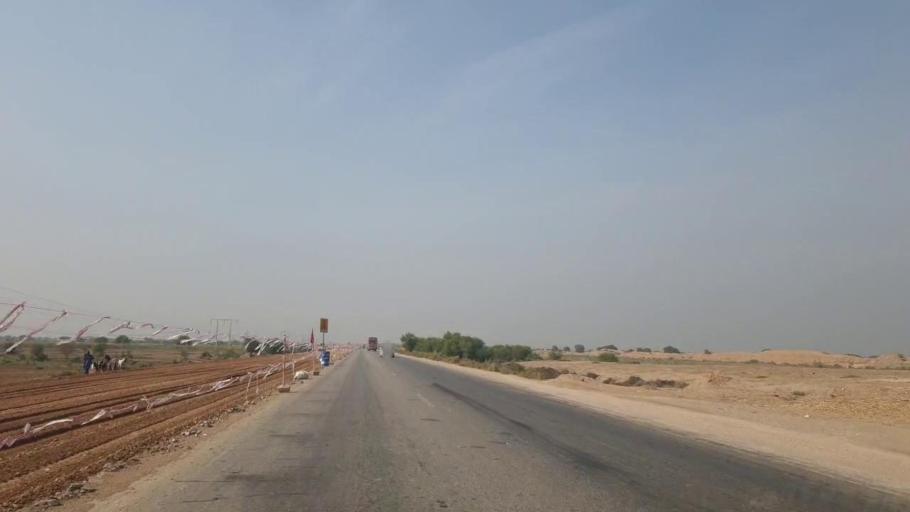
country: PK
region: Sindh
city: Sann
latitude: 26.1454
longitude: 68.0337
